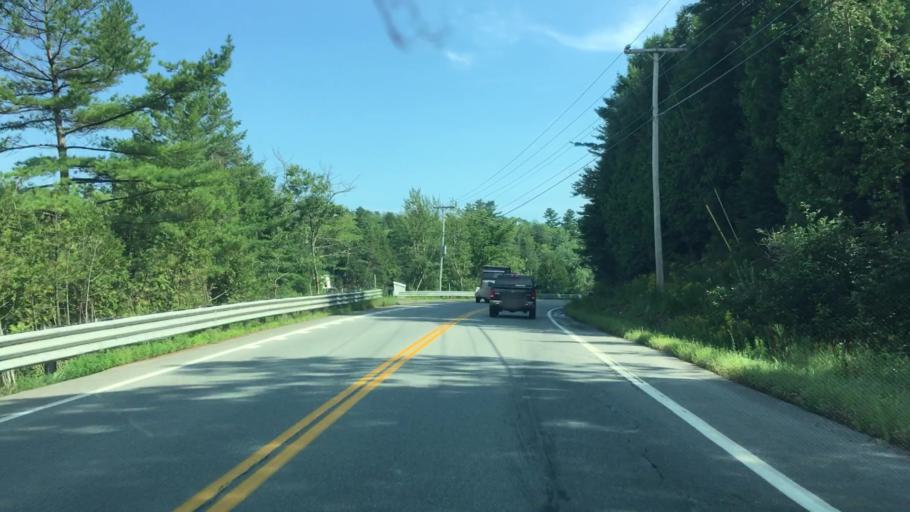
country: US
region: Maine
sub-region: Waldo County
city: Frankfort
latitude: 44.6027
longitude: -68.8688
